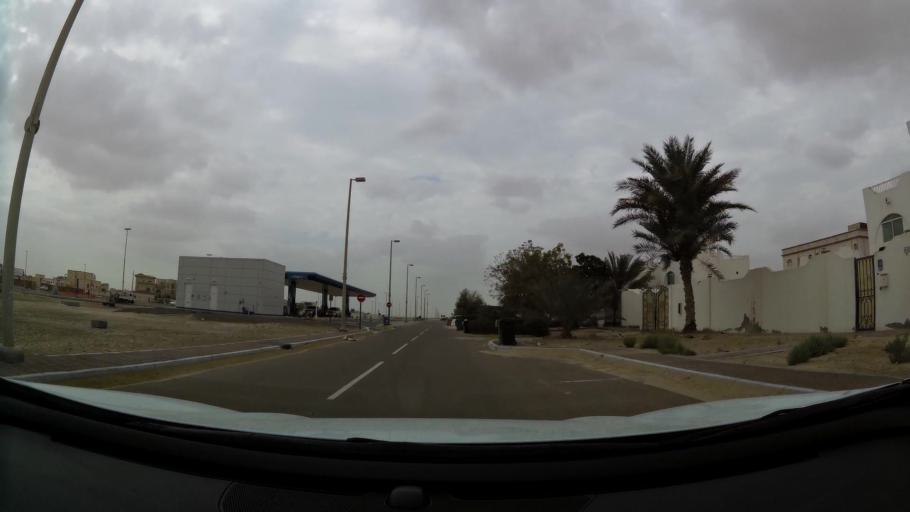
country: AE
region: Abu Dhabi
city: Abu Dhabi
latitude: 24.3845
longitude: 54.6483
